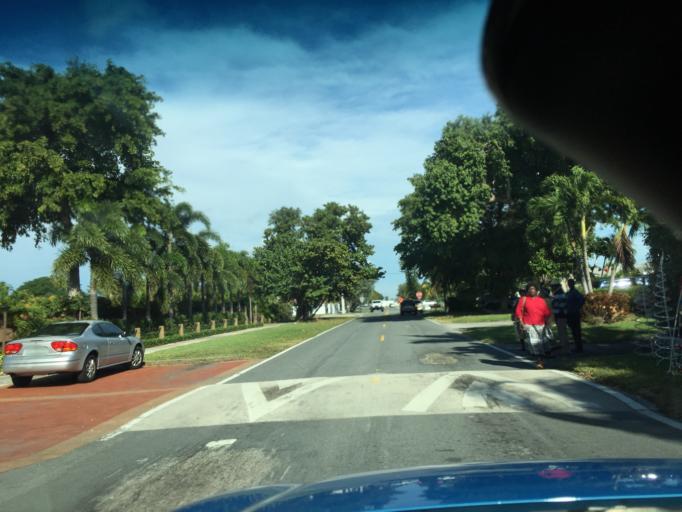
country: US
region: Florida
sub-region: Broward County
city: Pompano Beach
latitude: 26.2376
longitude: -80.1128
